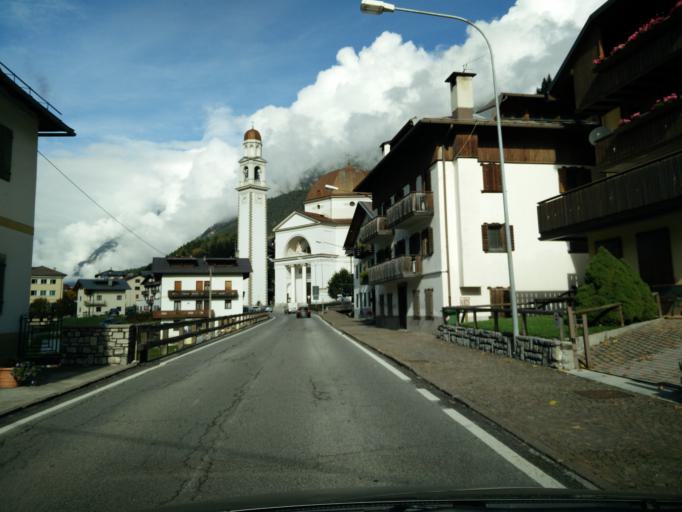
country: IT
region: Veneto
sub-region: Provincia di Belluno
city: Auronzo
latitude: 46.5445
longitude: 12.4588
